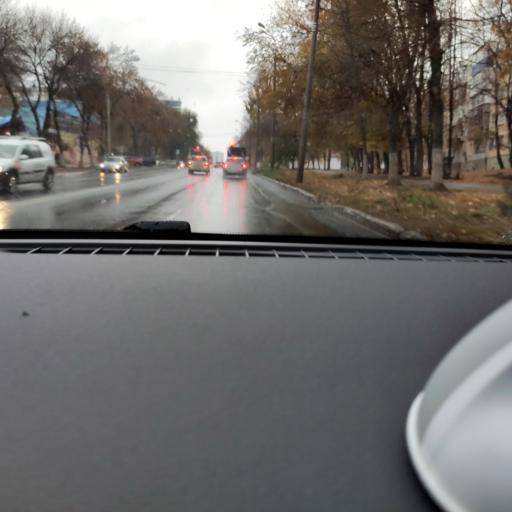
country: RU
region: Samara
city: Samara
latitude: 53.2523
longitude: 50.2365
